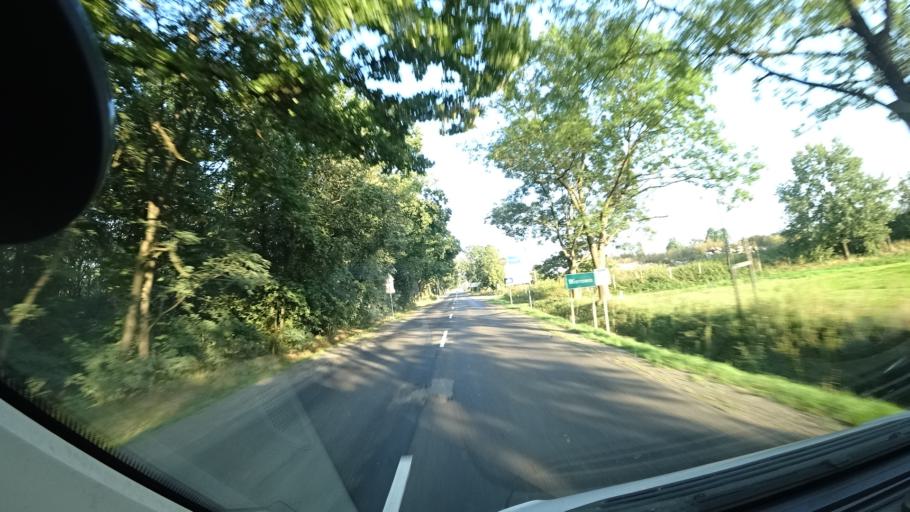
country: PL
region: Opole Voivodeship
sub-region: Powiat kedzierzynsko-kozielski
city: Bierawa
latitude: 50.2936
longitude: 18.2478
